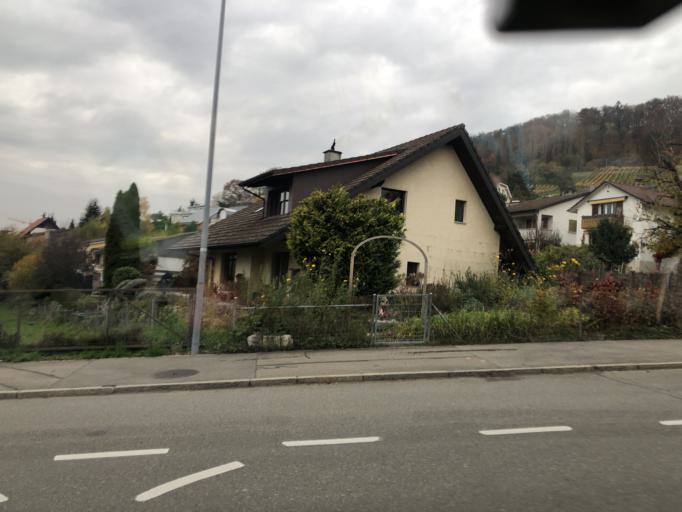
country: CH
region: Aargau
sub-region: Bezirk Baden
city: Neuenhof
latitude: 47.4691
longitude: 8.3385
